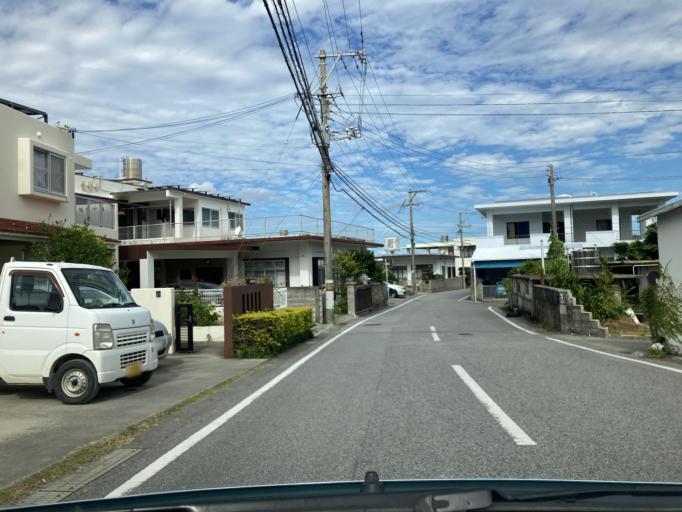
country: JP
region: Okinawa
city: Ishikawa
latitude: 26.4295
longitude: 127.7772
